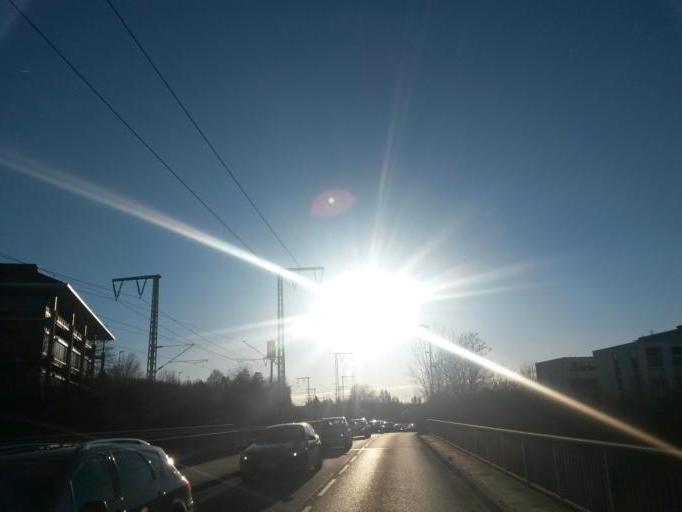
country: DE
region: Baden-Wuerttemberg
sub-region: Regierungsbezirk Stuttgart
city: Boeblingen
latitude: 48.6775
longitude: 8.9757
